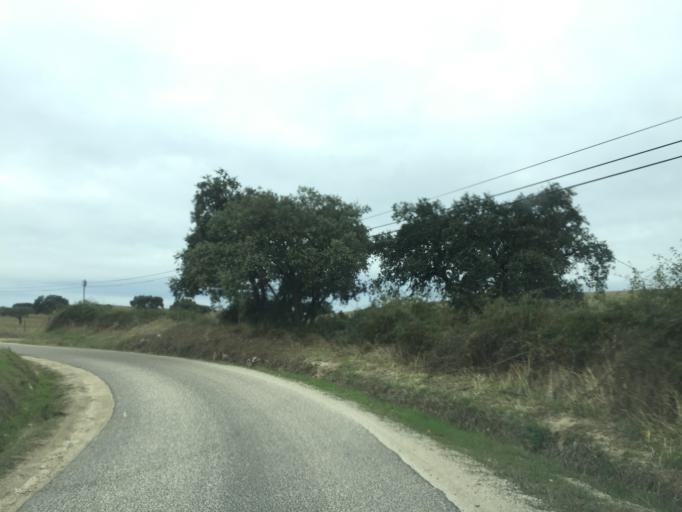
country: PT
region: Portalegre
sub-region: Avis
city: Avis
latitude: 39.0523
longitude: -7.7948
